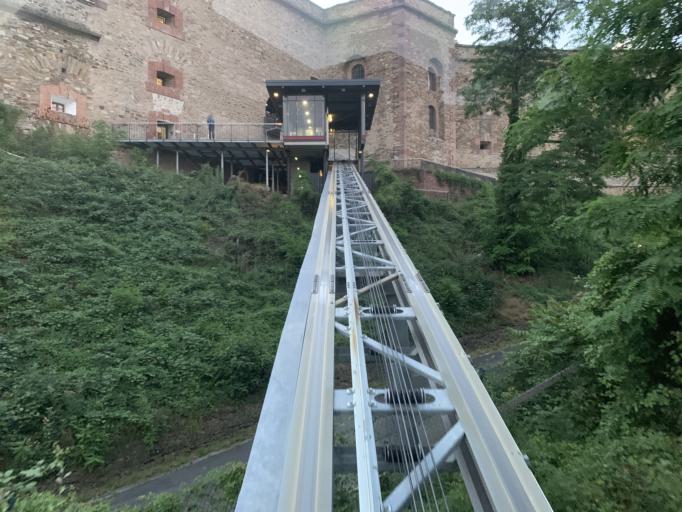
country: DE
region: Rheinland-Pfalz
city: Urbar
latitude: 50.3626
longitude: 7.6143
